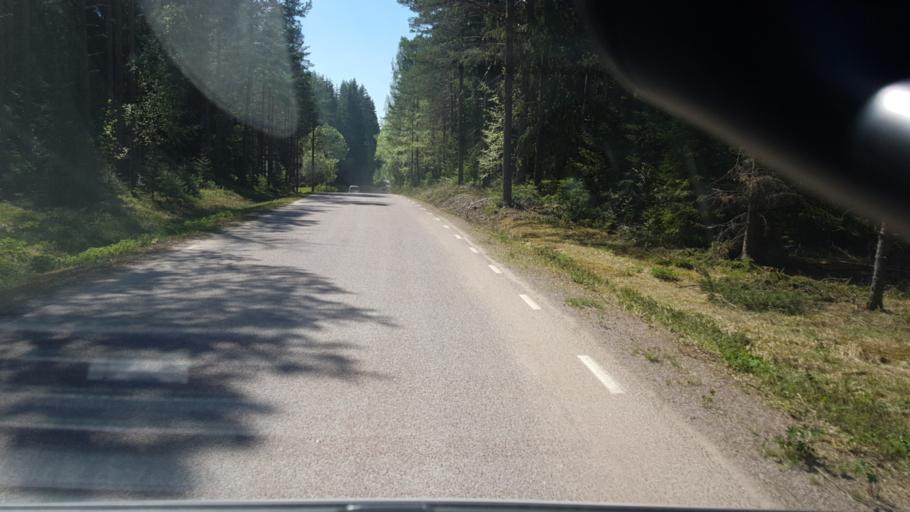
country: SE
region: Vaermland
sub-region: Arvika Kommun
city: Arvika
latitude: 59.7818
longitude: 12.8325
